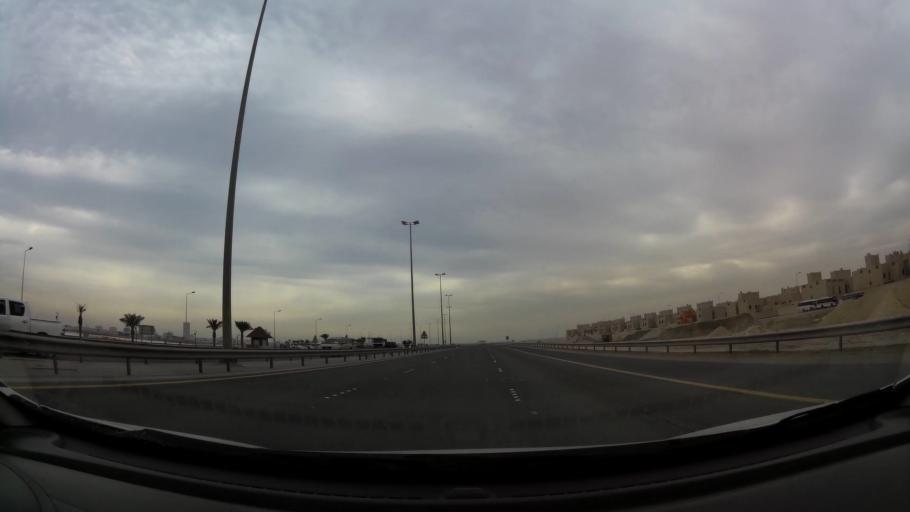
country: BH
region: Manama
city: Manama
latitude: 26.1819
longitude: 50.5910
